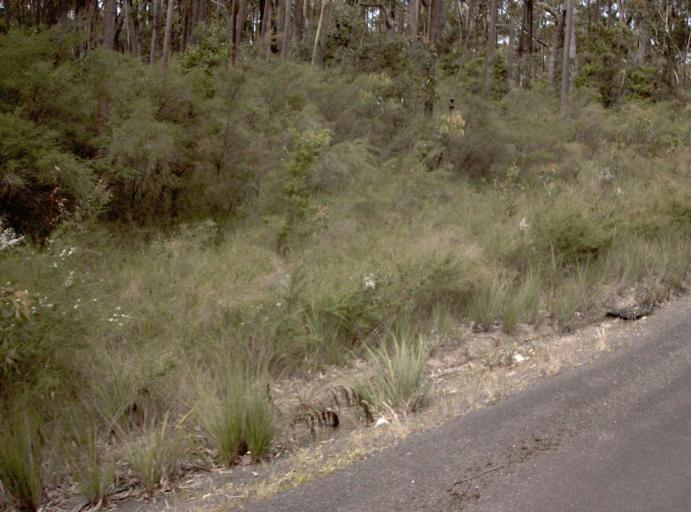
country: AU
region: New South Wales
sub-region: Bega Valley
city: Eden
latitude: -37.5083
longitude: 149.5210
